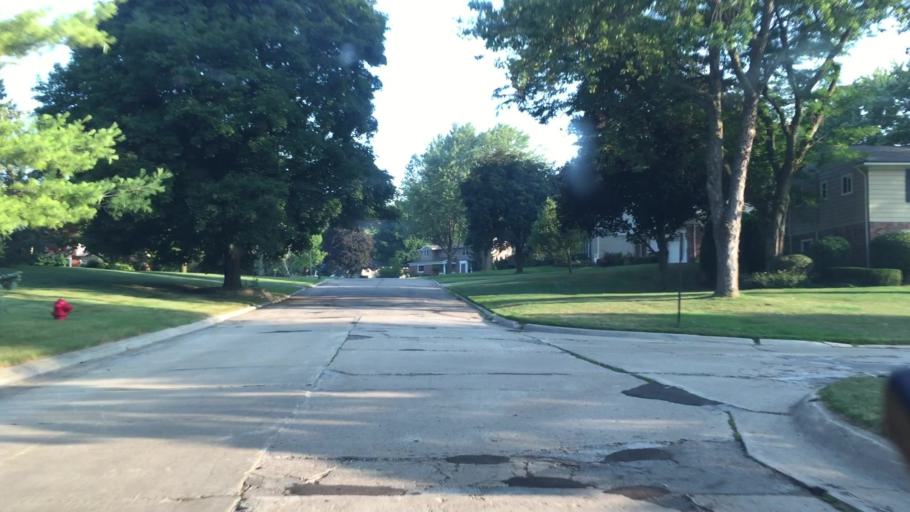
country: US
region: Michigan
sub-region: Oakland County
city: Bloomfield Hills
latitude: 42.5991
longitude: -83.2809
